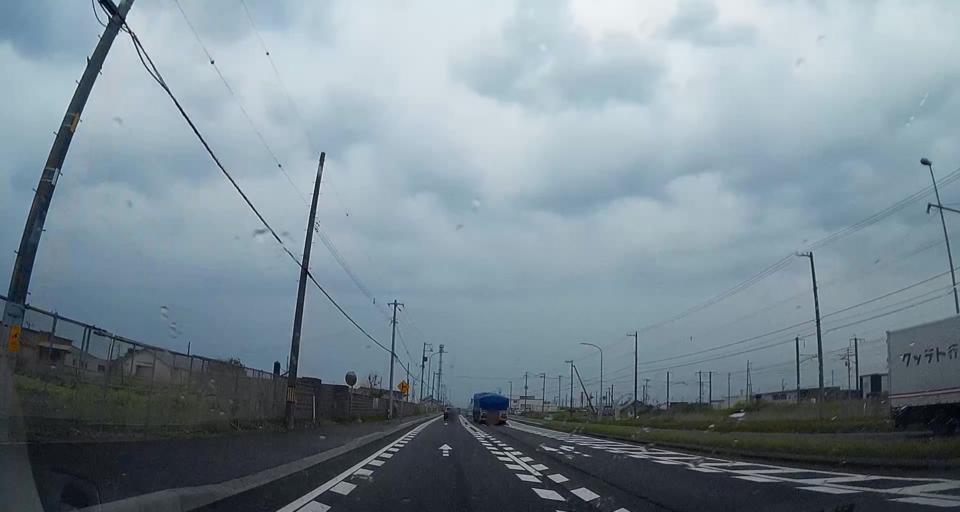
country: JP
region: Hokkaido
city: Tomakomai
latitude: 42.6091
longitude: 141.5078
